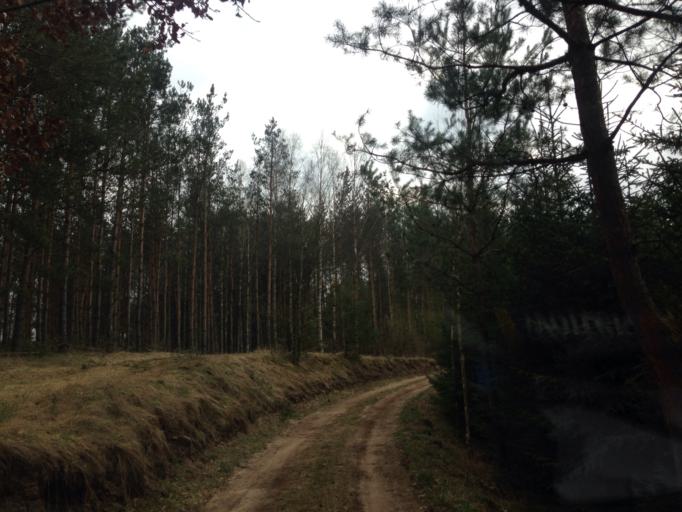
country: PL
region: Warmian-Masurian Voivodeship
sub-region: Powiat dzialdowski
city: Lidzbark
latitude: 53.3742
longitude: 19.7637
